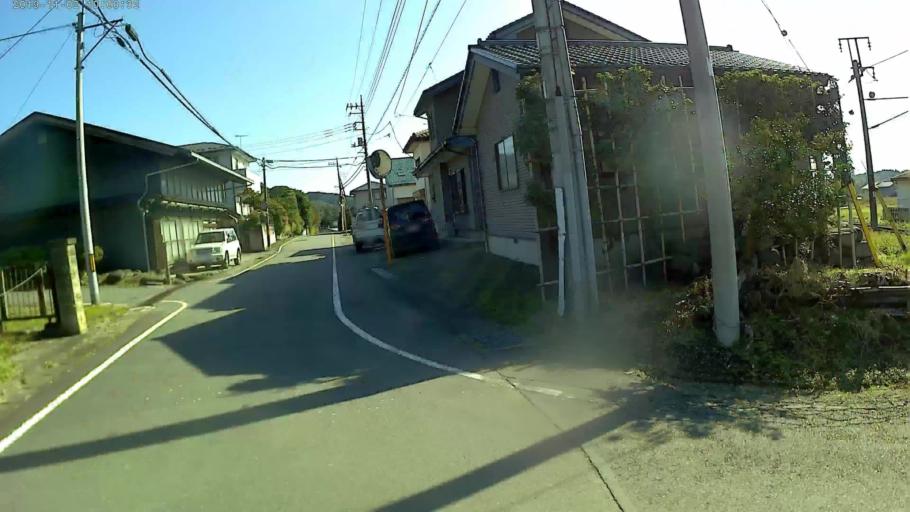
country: JP
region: Gunma
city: Annaka
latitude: 36.3188
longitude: 138.7826
